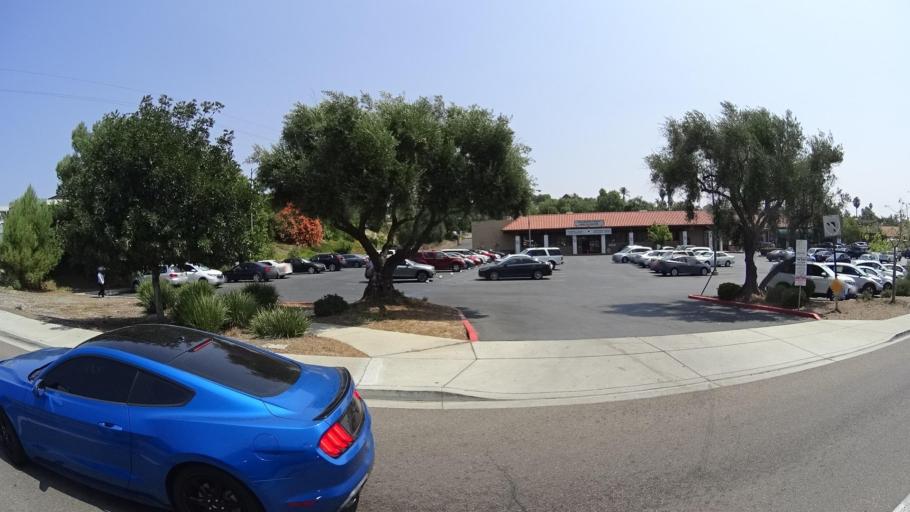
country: US
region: California
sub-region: San Diego County
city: Fallbrook
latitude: 33.3690
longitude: -117.2509
